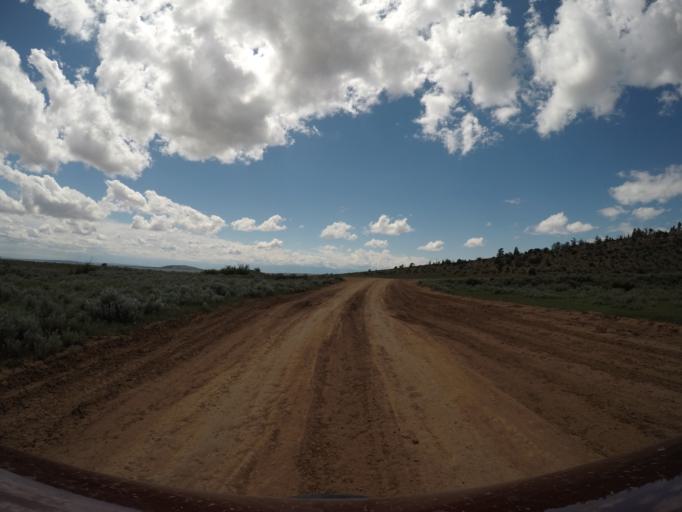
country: US
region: Montana
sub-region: Yellowstone County
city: Laurel
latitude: 45.2403
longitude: -108.6710
